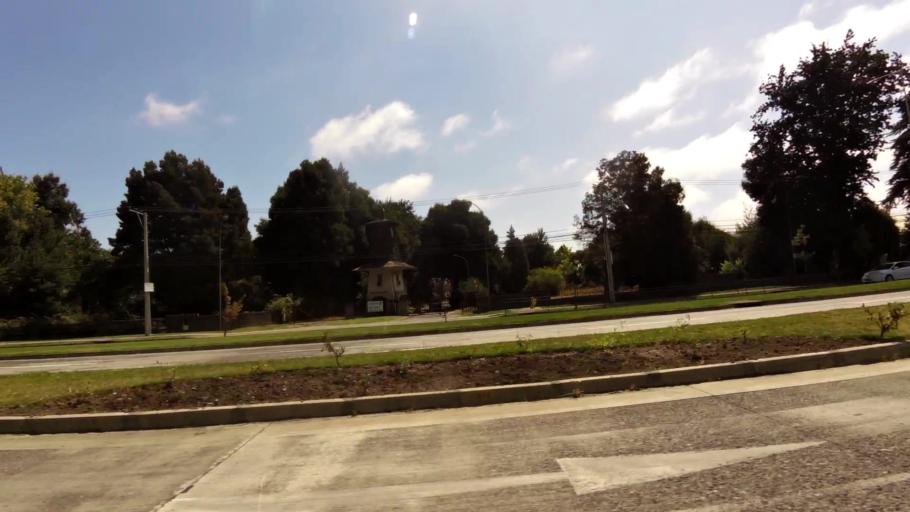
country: CL
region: Biobio
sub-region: Provincia de Concepcion
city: Concepcion
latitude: -36.7854
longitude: -73.0598
